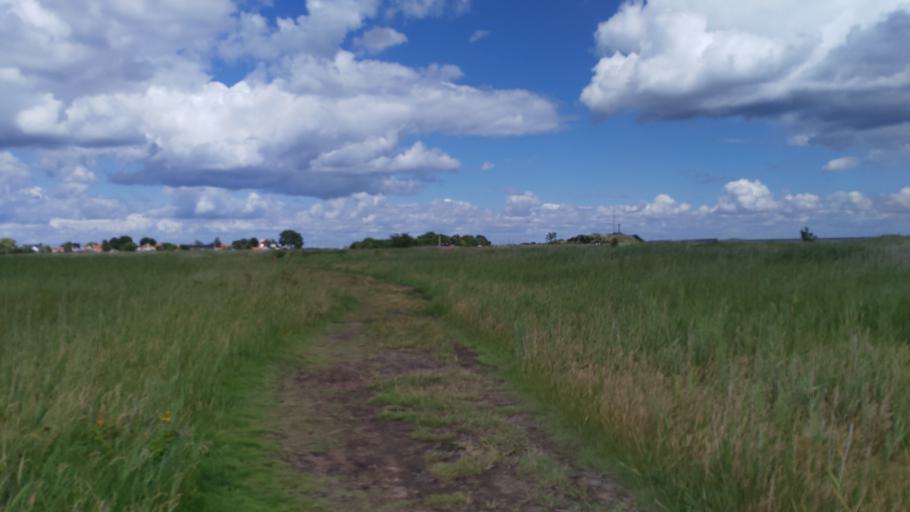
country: DK
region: Capital Region
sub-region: Dragor Kommune
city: Dragor
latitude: 55.5845
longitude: 12.6679
